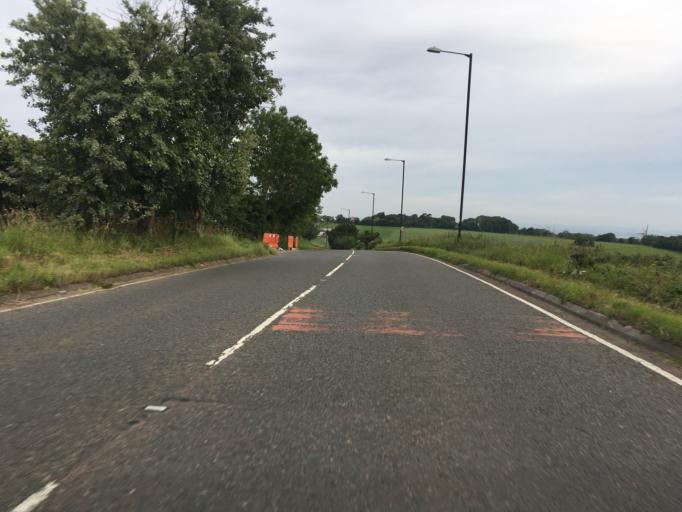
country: GB
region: England
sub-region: North Somerset
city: Easton-in-Gordano
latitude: 51.4704
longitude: -2.6842
